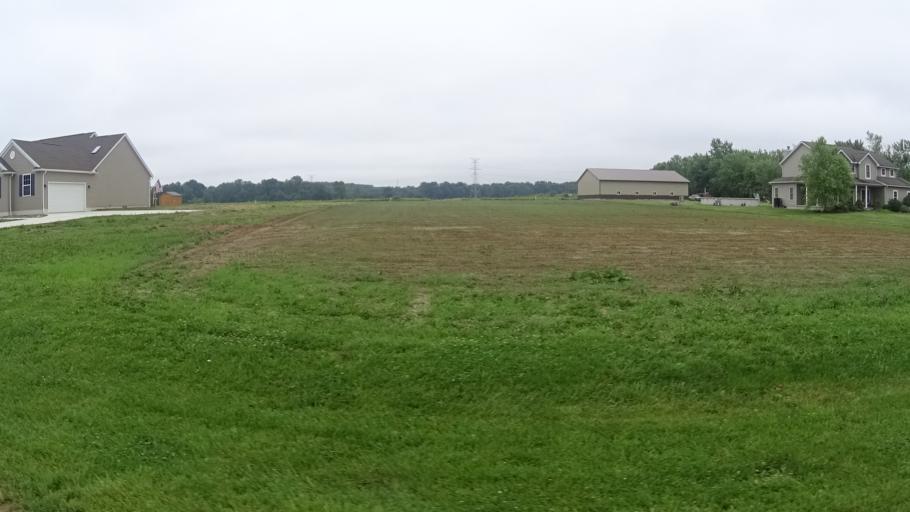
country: US
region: Ohio
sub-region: Erie County
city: Huron
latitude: 41.3402
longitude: -82.5639
